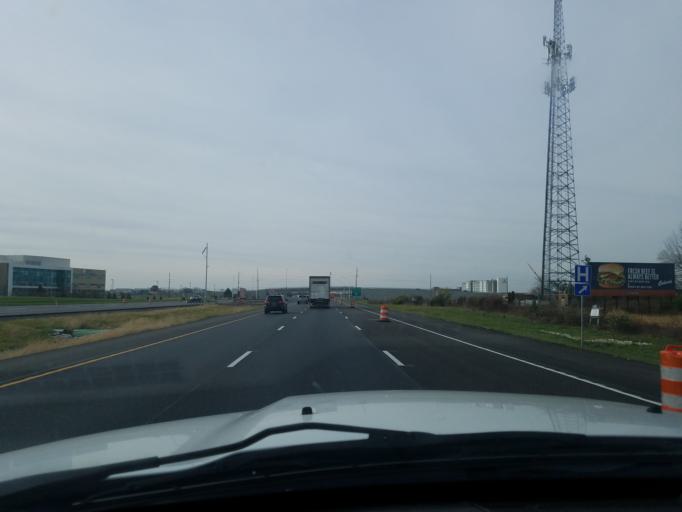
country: US
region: Indiana
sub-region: Hancock County
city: McCordsville
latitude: 39.9912
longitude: -85.9134
